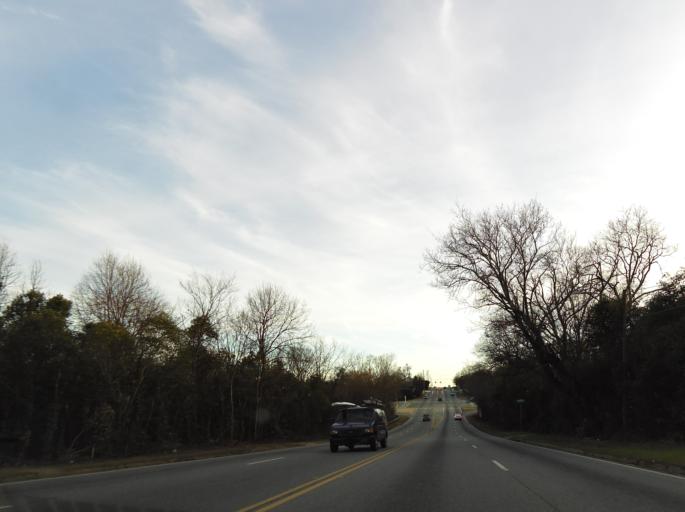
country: US
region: Georgia
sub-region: Bibb County
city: Macon
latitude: 32.8157
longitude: -83.6400
